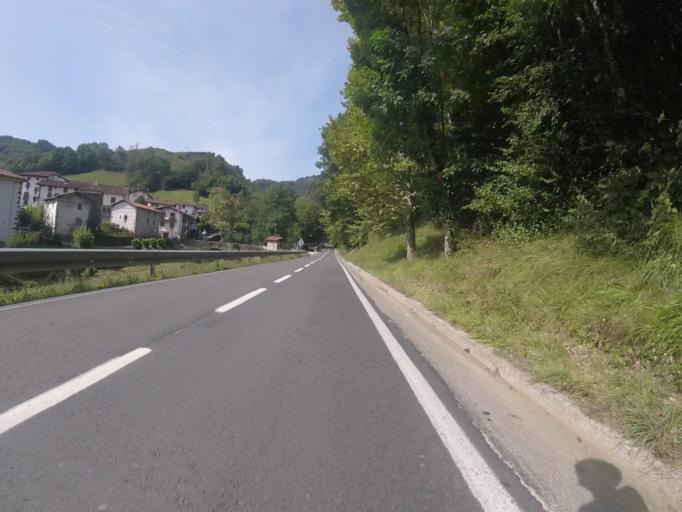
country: ES
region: Navarre
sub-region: Provincia de Navarra
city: Zubieta
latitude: 43.1262
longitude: -1.7418
